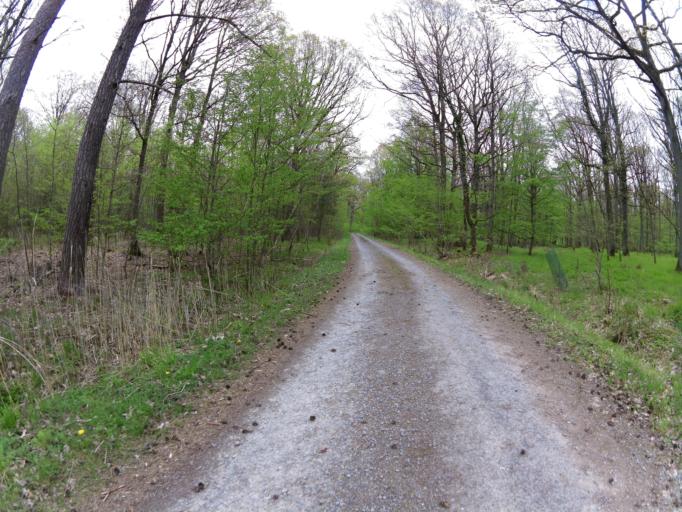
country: DE
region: Bavaria
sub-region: Regierungsbezirk Unterfranken
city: Prosselsheim
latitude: 49.8562
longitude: 10.1561
